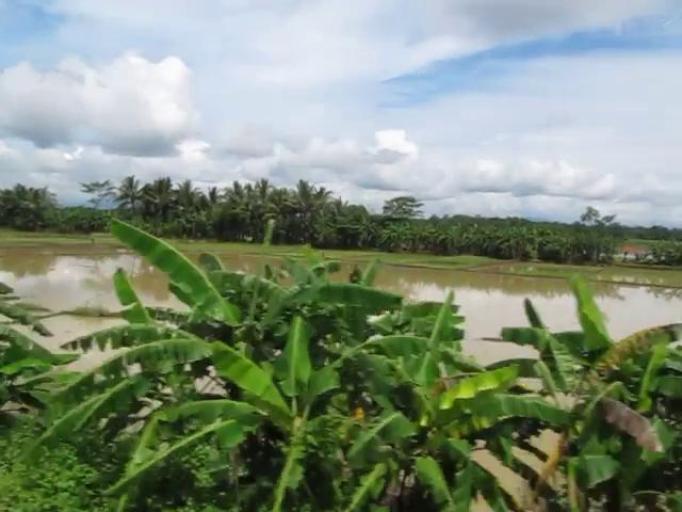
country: ID
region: Central Java
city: Meluwung
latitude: -7.3833
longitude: 108.6930
